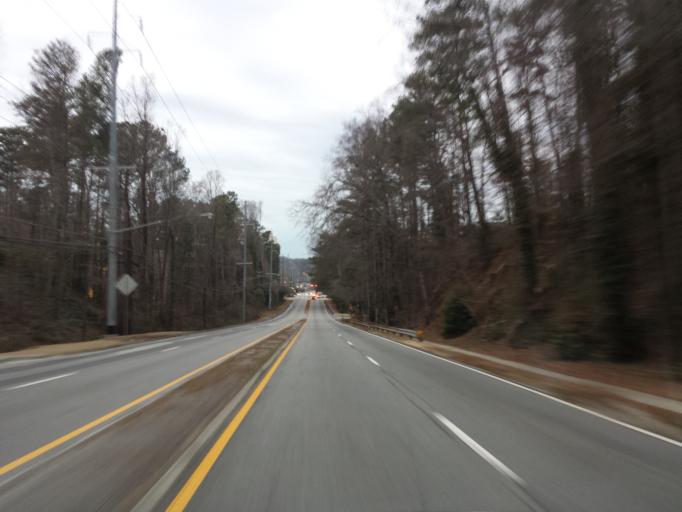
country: US
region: Georgia
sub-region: Cobb County
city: Vinings
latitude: 33.8421
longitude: -84.4218
